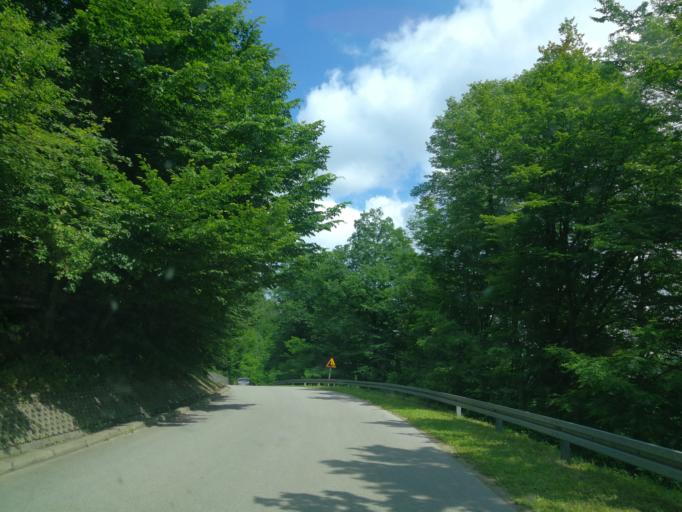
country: PL
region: Subcarpathian Voivodeship
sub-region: Powiat leski
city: Polanczyk
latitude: 49.4176
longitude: 22.4339
